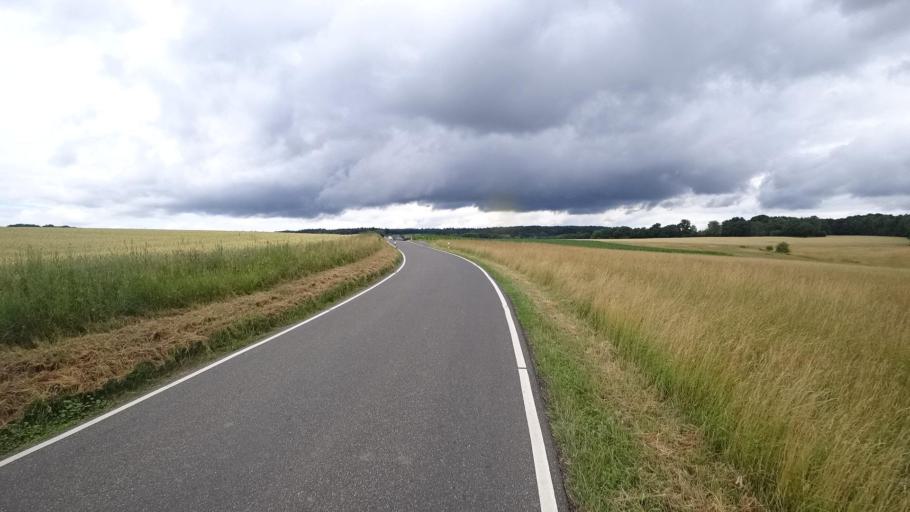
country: DE
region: Rheinland-Pfalz
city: Mehren
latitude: 50.6907
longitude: 7.5030
